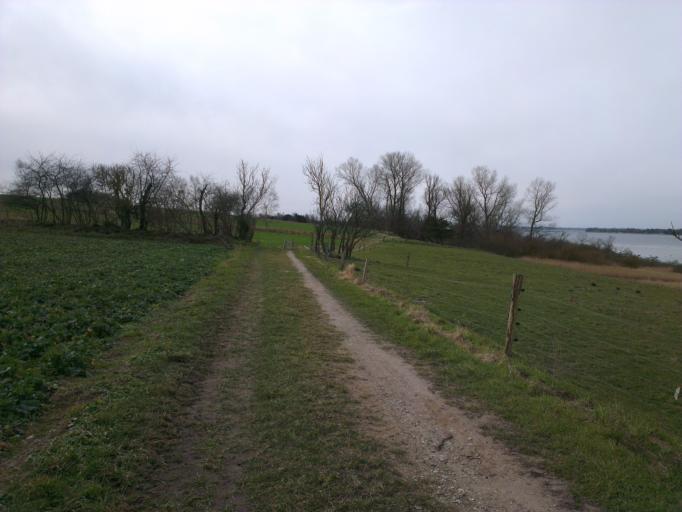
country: DK
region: Zealand
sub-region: Lejre Kommune
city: Ejby
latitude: 55.7774
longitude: 11.8634
